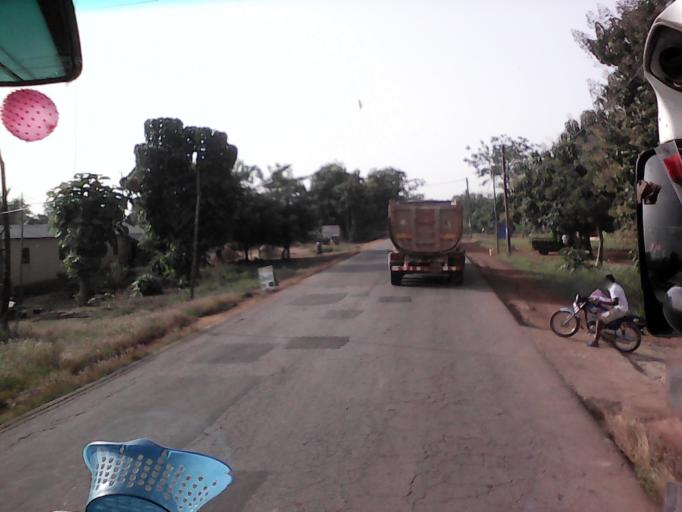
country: TG
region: Kara
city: Kara
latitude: 9.5042
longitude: 1.2090
